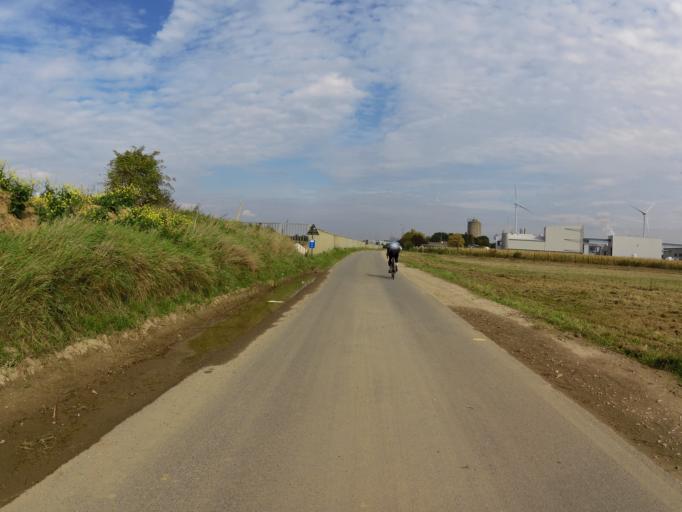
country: BE
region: Flanders
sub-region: Provincie Limburg
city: Lanaken
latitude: 50.8774
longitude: 5.6456
